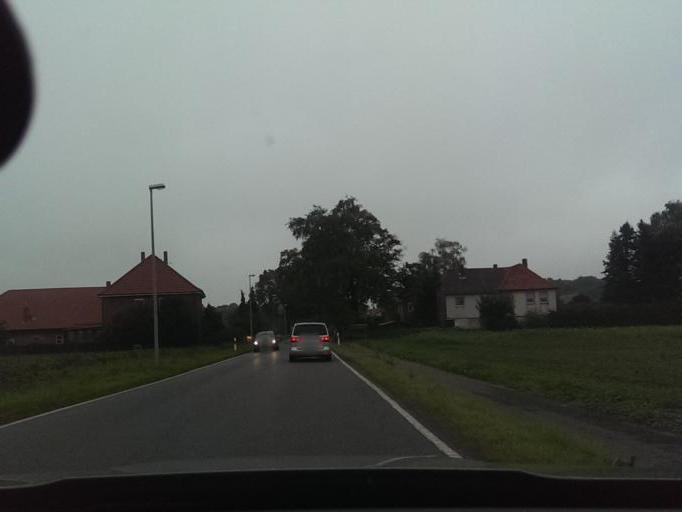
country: DE
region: Lower Saxony
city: Garbsen-Mitte
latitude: 52.4463
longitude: 9.6472
